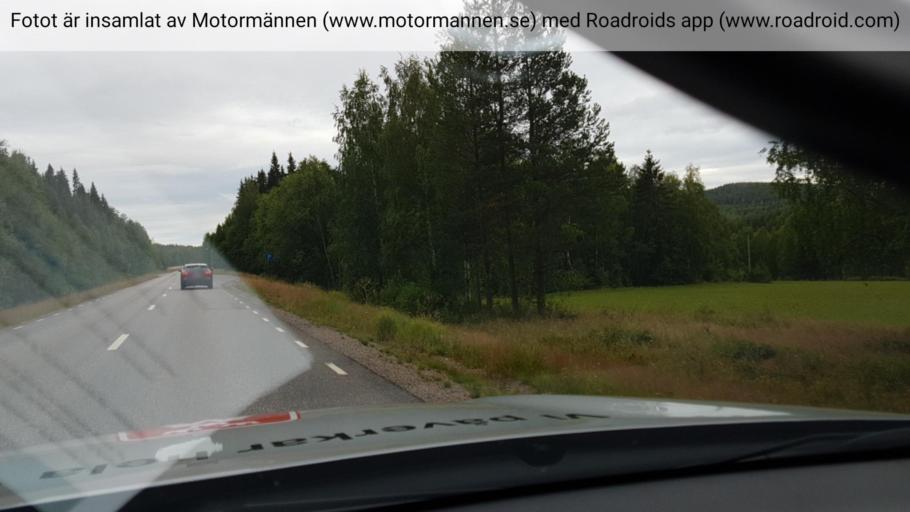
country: SE
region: Norrbotten
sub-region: Overkalix Kommun
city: OEverkalix
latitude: 66.5588
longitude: 22.7604
